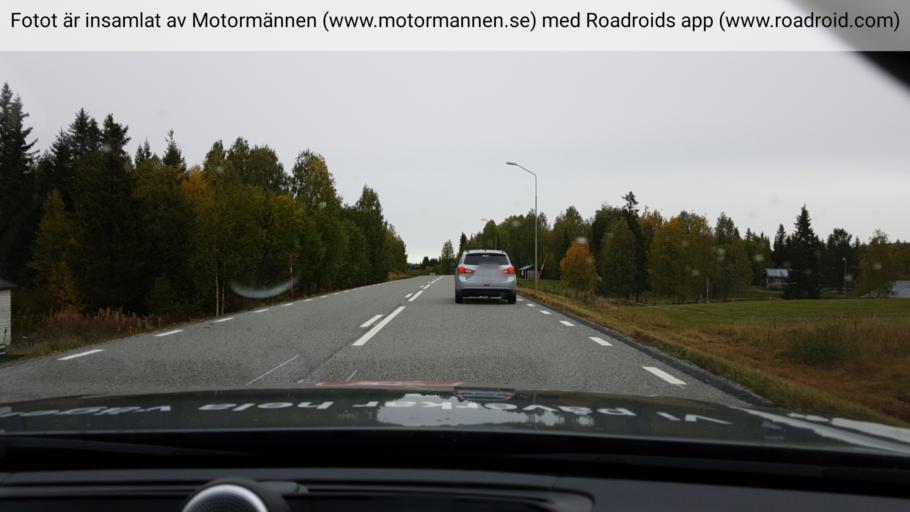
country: SE
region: Jaemtland
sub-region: Stroemsunds Kommun
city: Stroemsund
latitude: 64.0553
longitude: 15.5480
